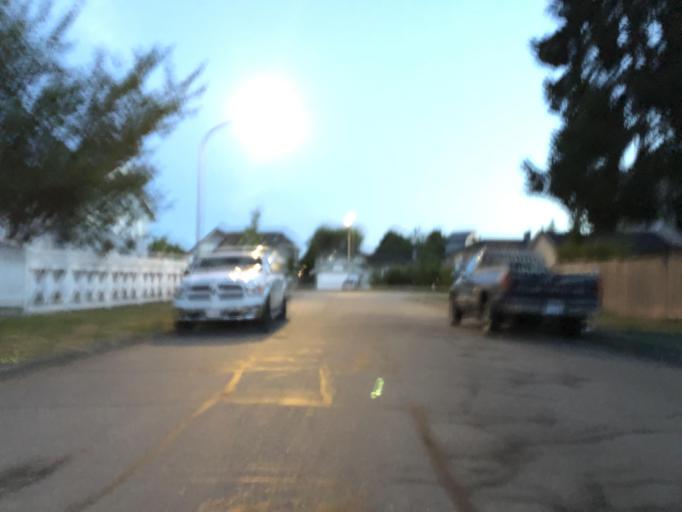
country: CA
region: British Columbia
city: Richmond
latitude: 49.1455
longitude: -123.1129
